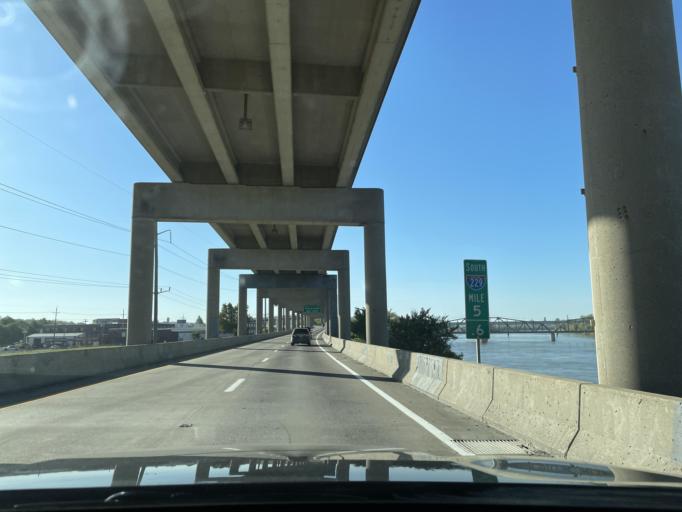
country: US
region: Missouri
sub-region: Buchanan County
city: Saint Joseph
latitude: 39.7588
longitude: -94.8570
